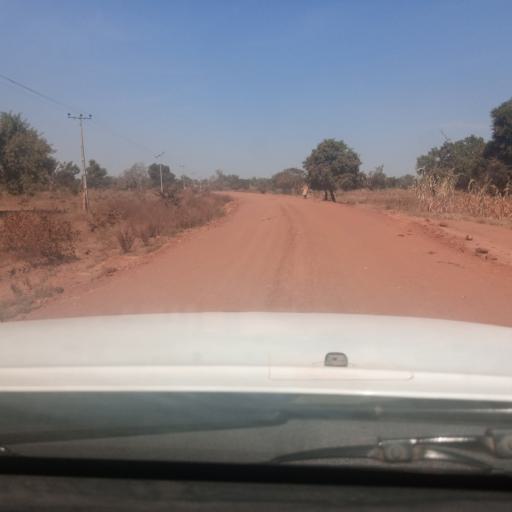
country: NG
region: Adamawa
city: Yola
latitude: 9.2057
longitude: 12.8781
